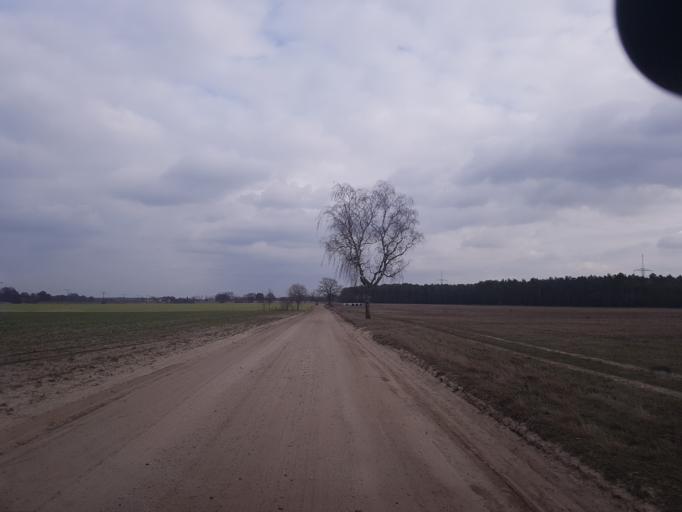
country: DE
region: Brandenburg
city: Sonnewalde
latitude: 51.6632
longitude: 13.6568
